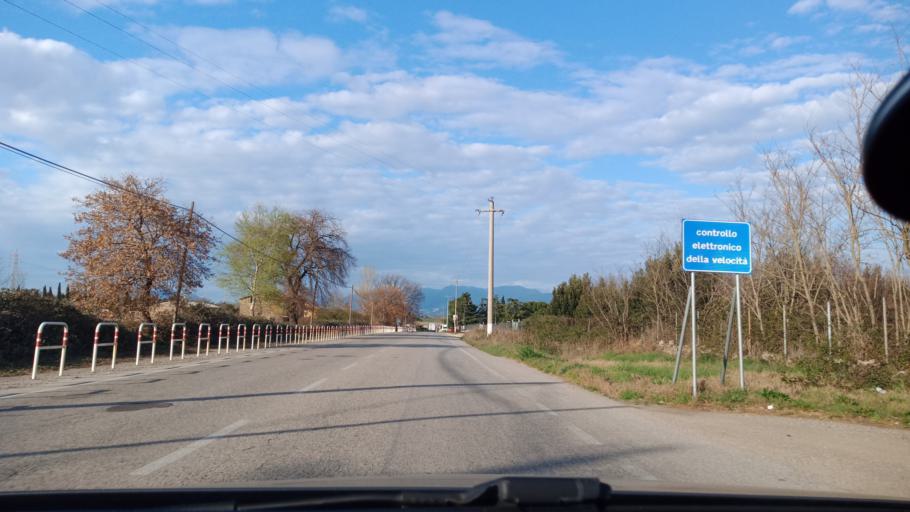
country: IT
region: Latium
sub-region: Citta metropolitana di Roma Capitale
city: Fiano Romano
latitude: 42.1564
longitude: 12.6174
